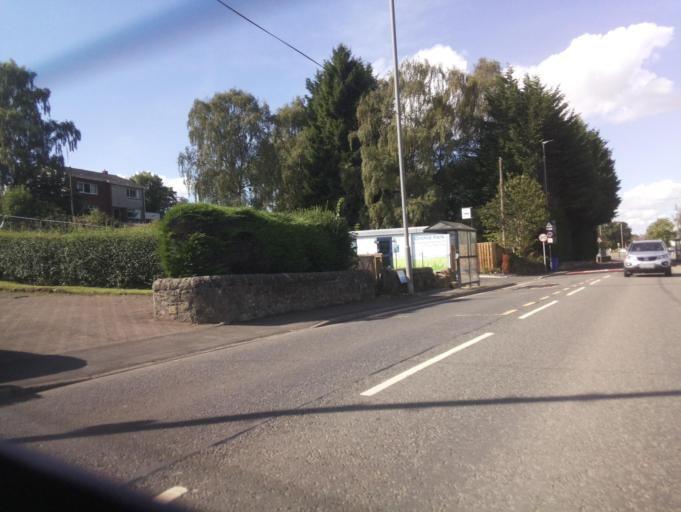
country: GB
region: Scotland
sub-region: Stirling
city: Plean
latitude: 56.0611
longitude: -3.8712
